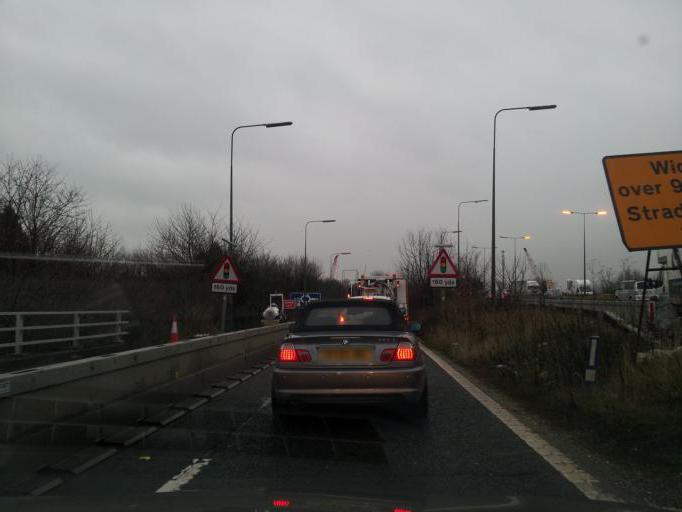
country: GB
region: England
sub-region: Manchester
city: Swinton
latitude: 53.4783
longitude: -2.3744
